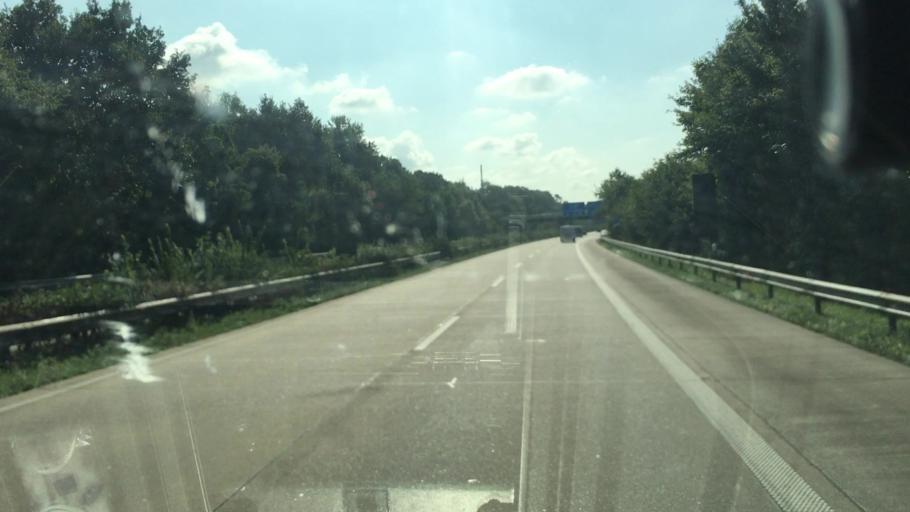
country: DE
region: Lower Saxony
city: Rastede
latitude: 53.2170
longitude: 8.2149
